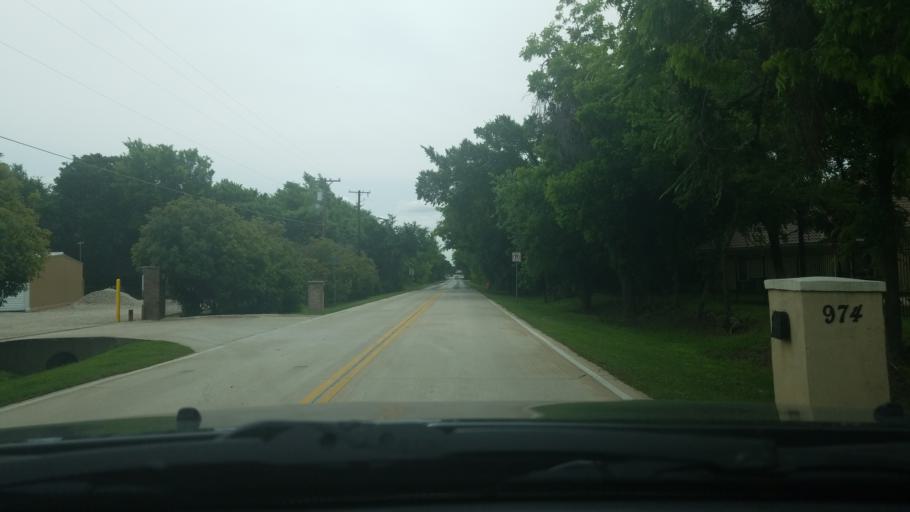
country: US
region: Texas
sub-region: Denton County
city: Lake Dallas
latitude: 33.1080
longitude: -97.0083
